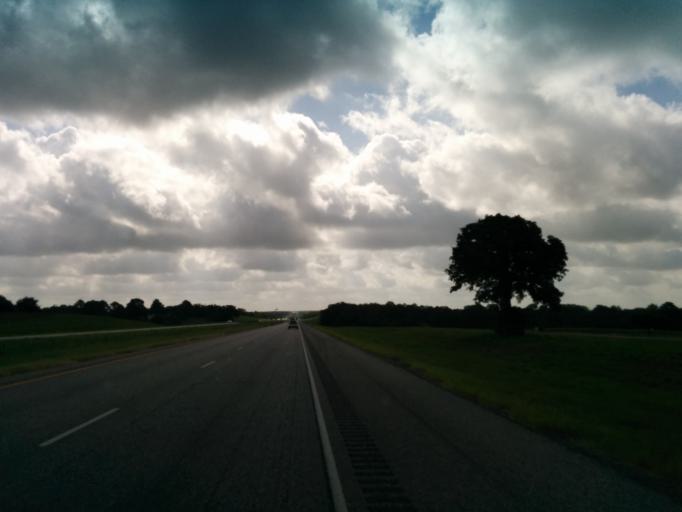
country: US
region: Texas
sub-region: Caldwell County
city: Luling
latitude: 29.6529
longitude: -97.5490
